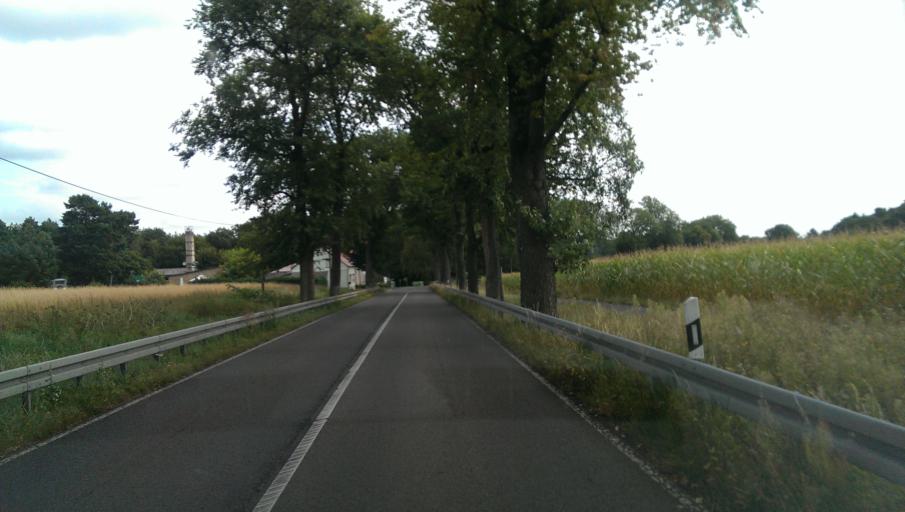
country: DE
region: Brandenburg
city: Trebbin
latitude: 52.1984
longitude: 13.2151
